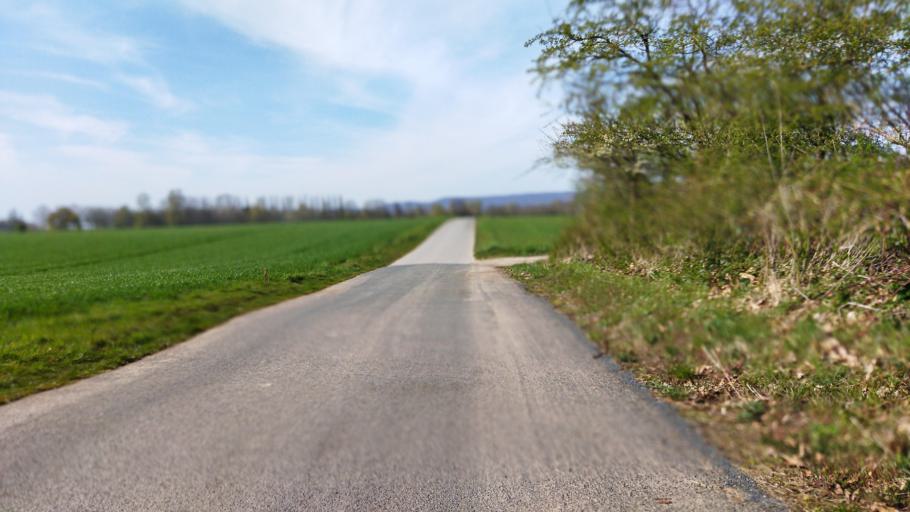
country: DE
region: Lower Saxony
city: Hessisch Oldendorf
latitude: 52.1429
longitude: 9.2849
